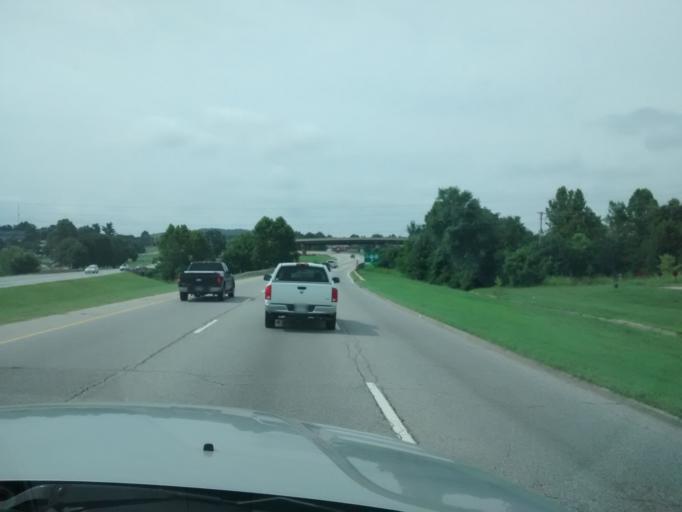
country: US
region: Arkansas
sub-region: Washington County
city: Johnson
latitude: 36.1211
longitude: -94.1451
